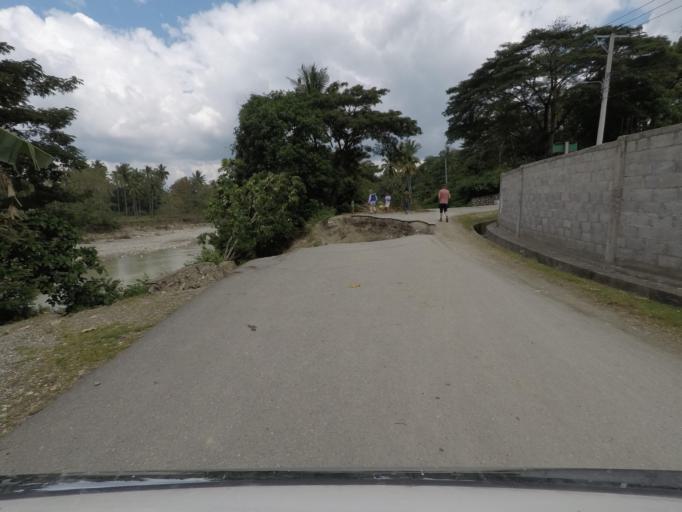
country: TL
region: Viqueque
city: Viqueque
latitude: -8.8728
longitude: 126.3646
